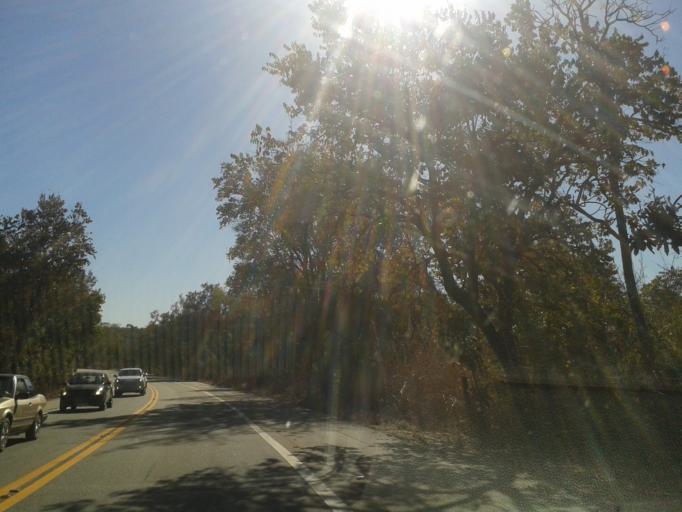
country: BR
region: Goias
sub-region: Itapuranga
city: Itapuranga
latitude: -15.4948
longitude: -50.3115
